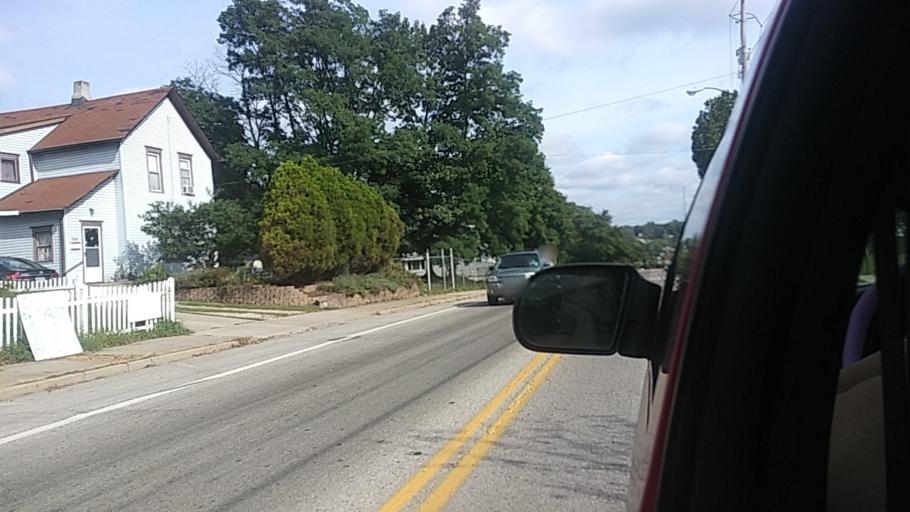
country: US
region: Ohio
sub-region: Summit County
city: Akron
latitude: 41.0819
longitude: -81.4904
